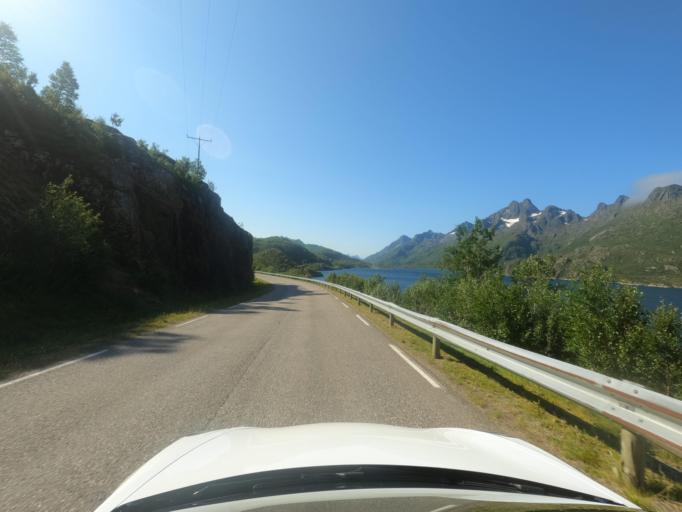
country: NO
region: Nordland
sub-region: Hadsel
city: Stokmarknes
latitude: 68.4490
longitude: 15.2033
